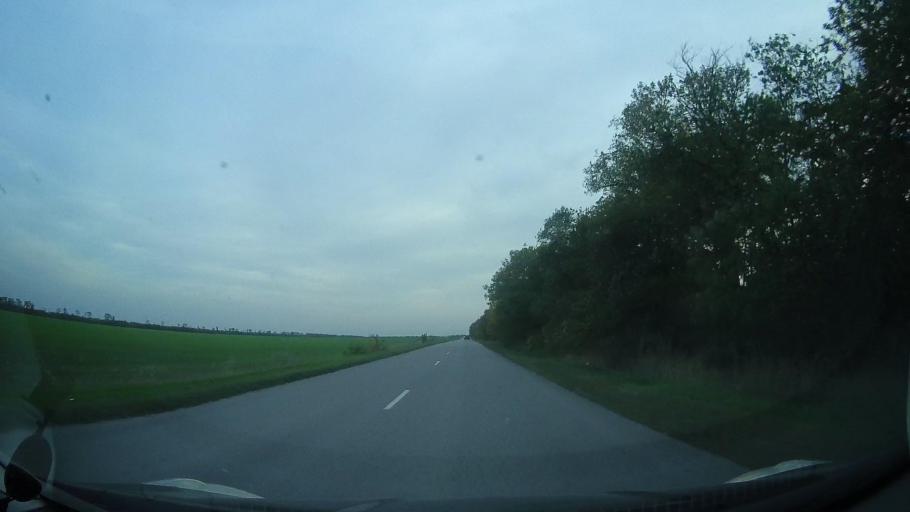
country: RU
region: Rostov
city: Kirovskaya
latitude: 47.0190
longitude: 39.9788
